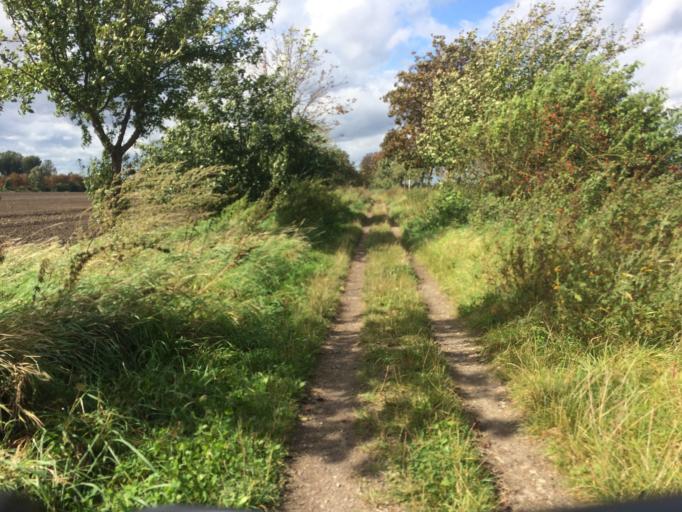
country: DE
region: Berlin
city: Blankenburg
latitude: 52.5835
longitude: 13.4575
